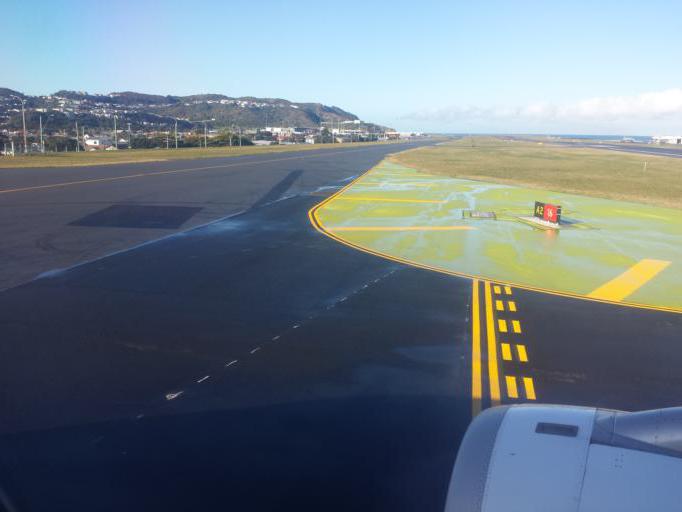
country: NZ
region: Wellington
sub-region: Wellington City
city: Wellington
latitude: -41.3190
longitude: 174.8084
